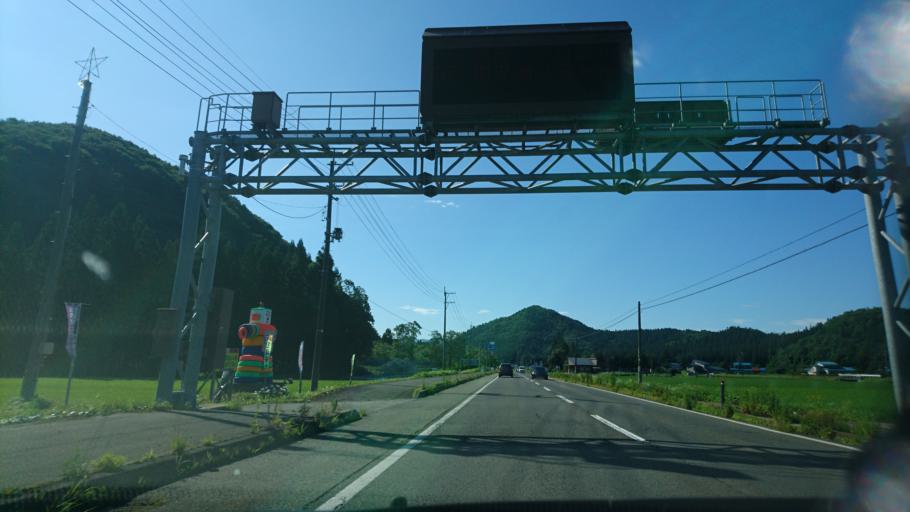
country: JP
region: Akita
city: Kakunodatemachi
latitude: 39.6054
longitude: 140.5168
